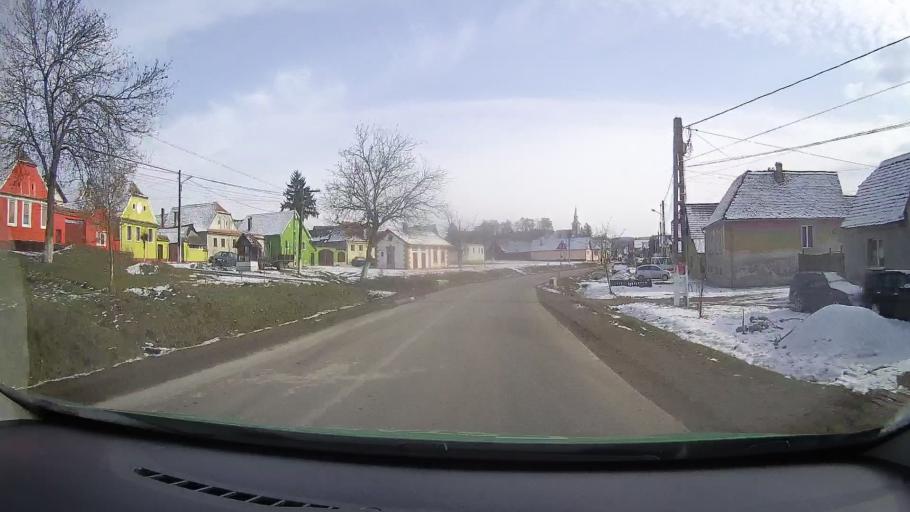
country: RO
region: Mures
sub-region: Comuna Apold
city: Saes
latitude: 46.1589
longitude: 24.7654
